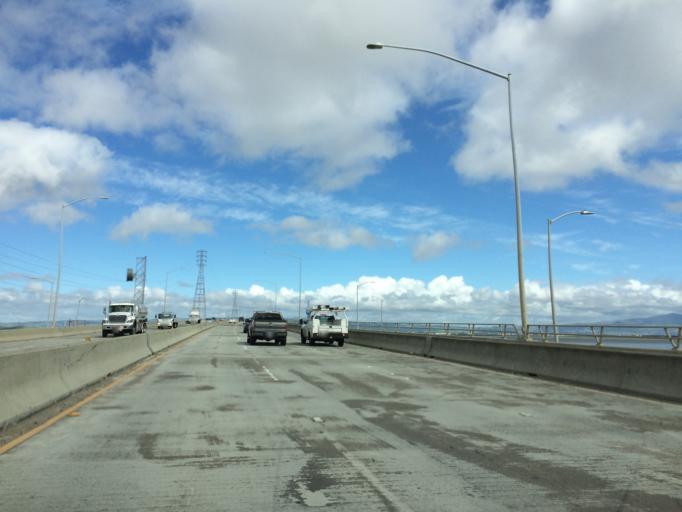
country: US
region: California
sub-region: San Mateo County
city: East Palo Alto
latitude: 37.4983
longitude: -122.1296
